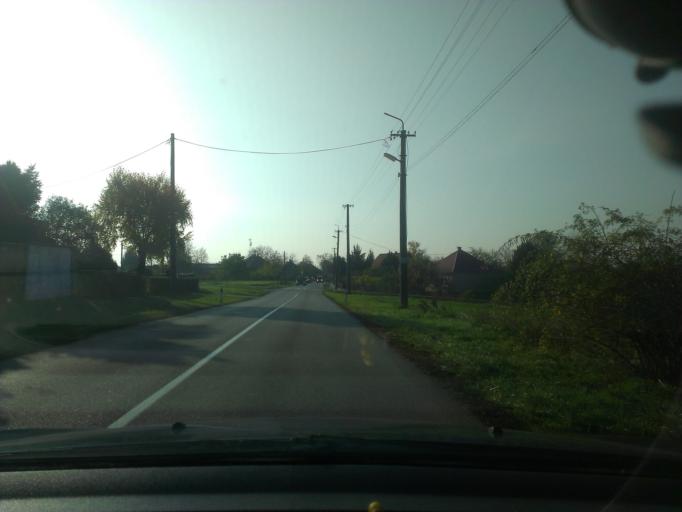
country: SK
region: Nitriansky
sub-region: Okres Nitra
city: Nitra
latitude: 48.4388
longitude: 17.9857
